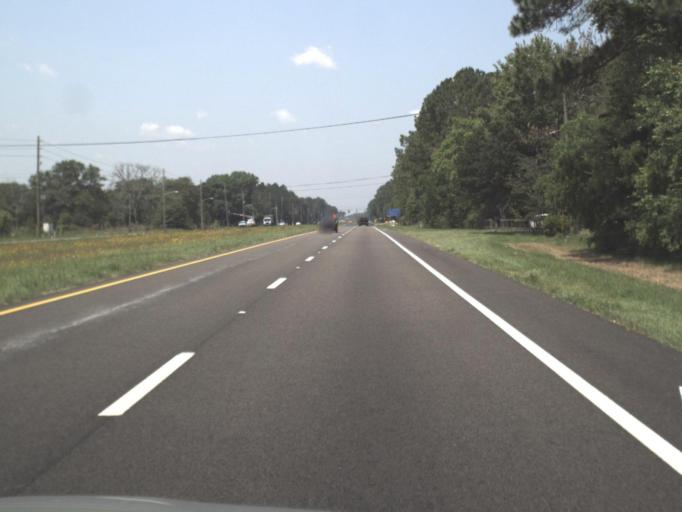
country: US
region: Florida
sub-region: Duval County
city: Baldwin
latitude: 30.2696
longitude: -81.8443
